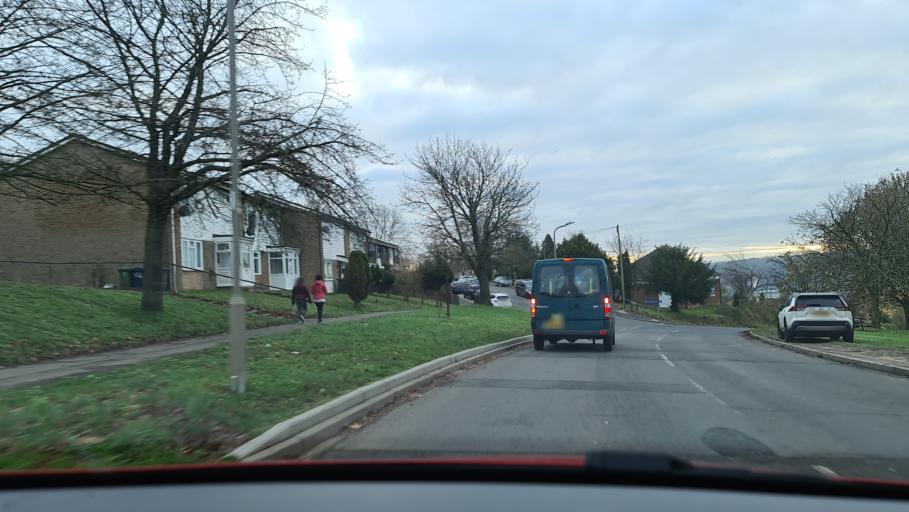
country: GB
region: England
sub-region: Buckinghamshire
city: High Wycombe
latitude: 51.6387
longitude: -0.7650
